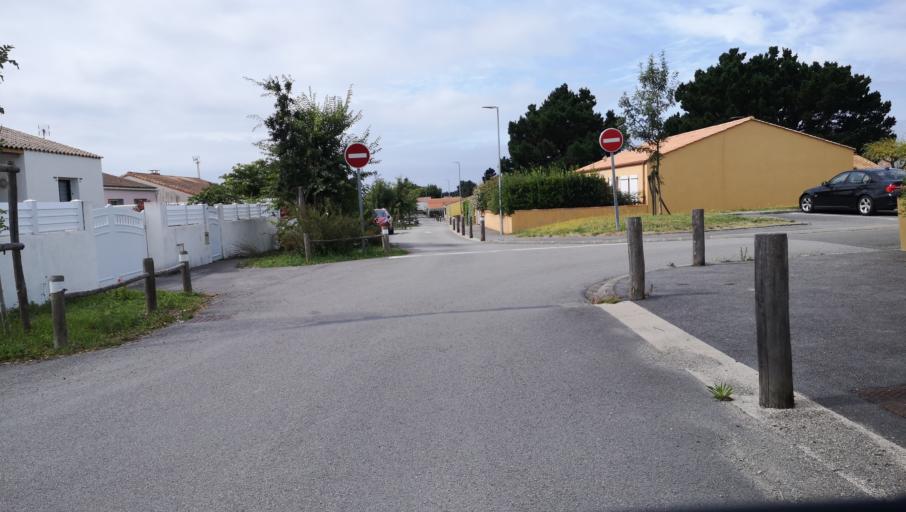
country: FR
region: Pays de la Loire
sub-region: Departement de la Vendee
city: Vaire
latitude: 46.5818
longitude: -1.7971
